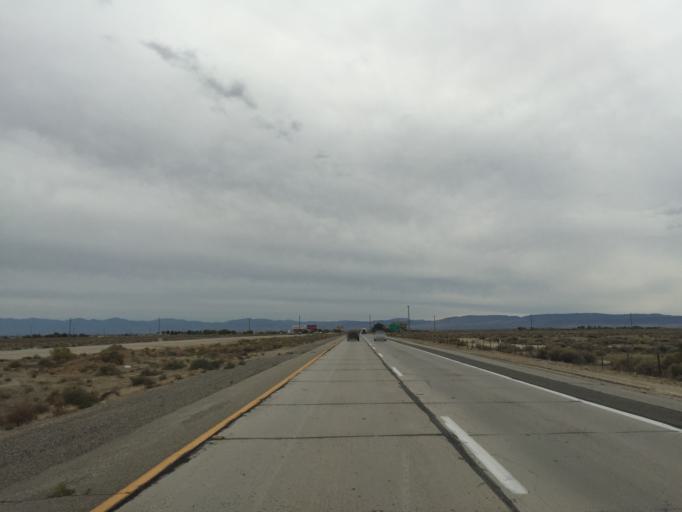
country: US
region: California
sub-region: Kern County
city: Rosamond
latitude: 34.8396
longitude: -118.1710
